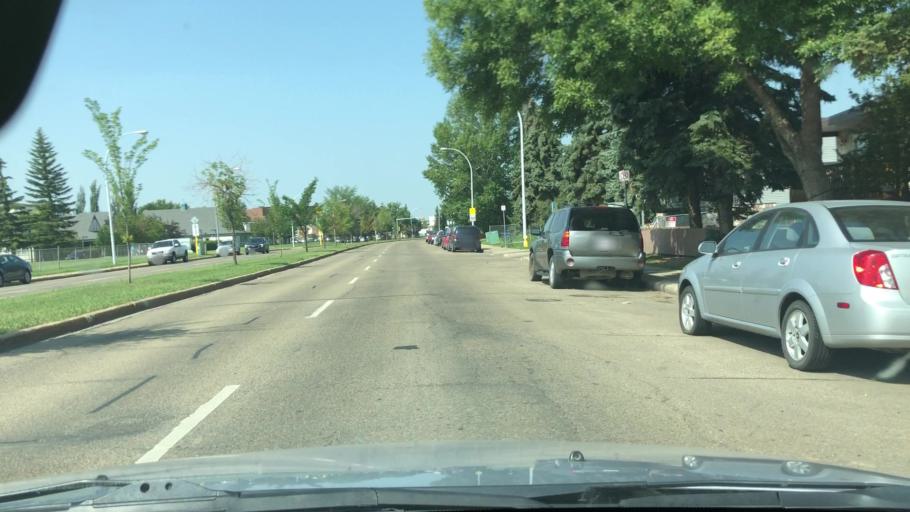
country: CA
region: Alberta
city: Edmonton
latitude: 53.6058
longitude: -113.4788
